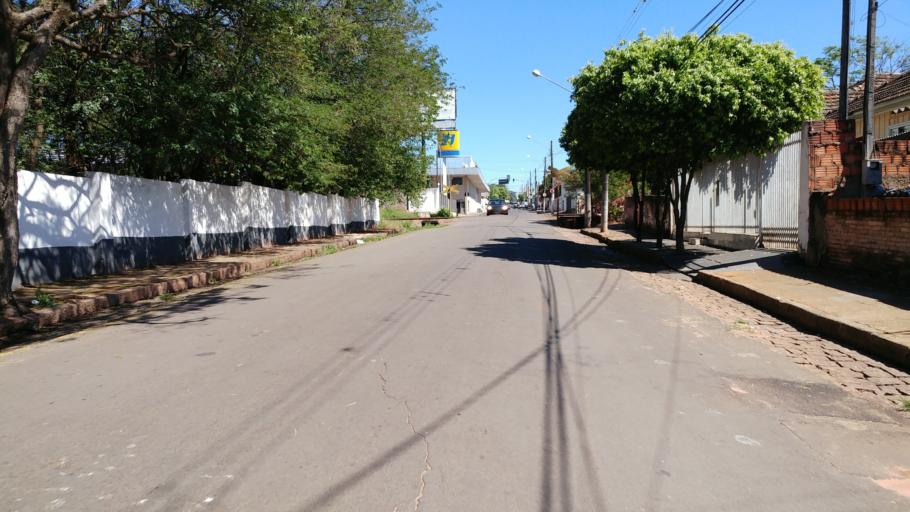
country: BR
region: Sao Paulo
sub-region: Paraguacu Paulista
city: Paraguacu Paulista
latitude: -22.4188
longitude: -50.5732
